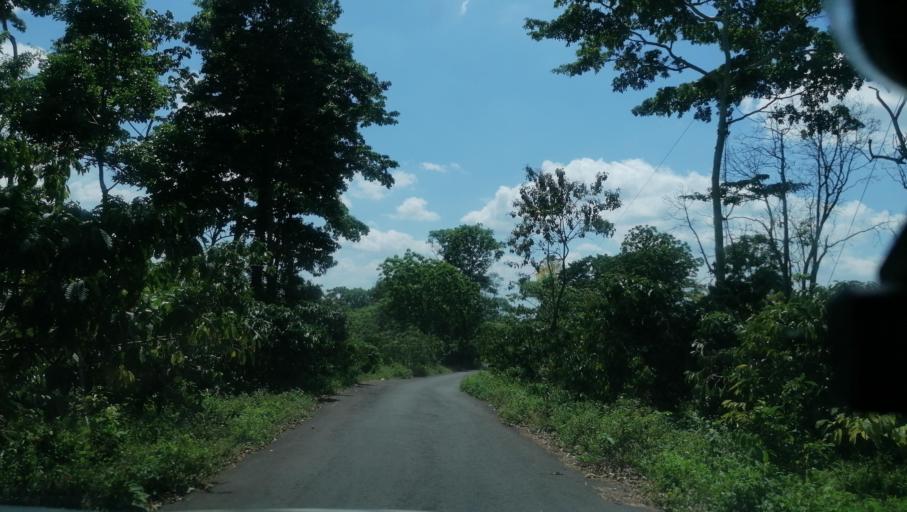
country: MX
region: Chiapas
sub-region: Cacahoatan
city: Benito Juarez
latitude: 15.0500
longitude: -92.1478
